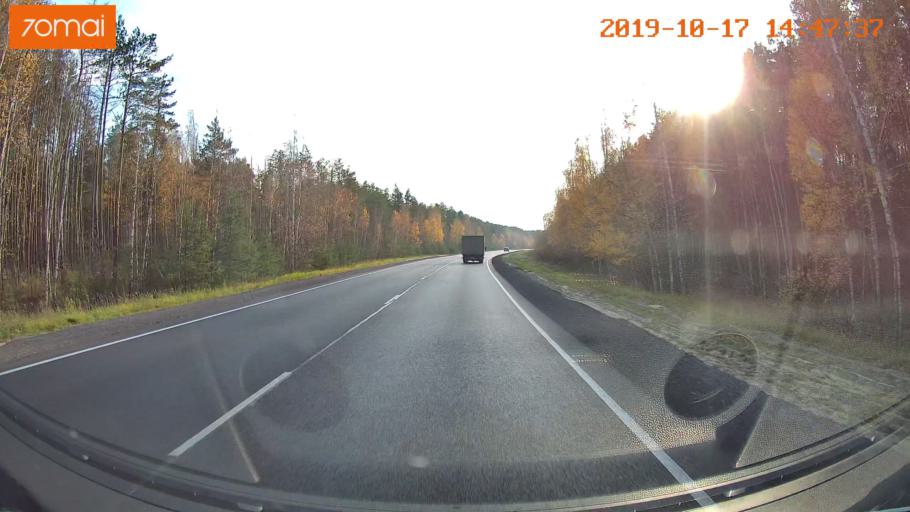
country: RU
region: Rjazan
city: Solotcha
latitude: 54.7690
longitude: 39.8591
